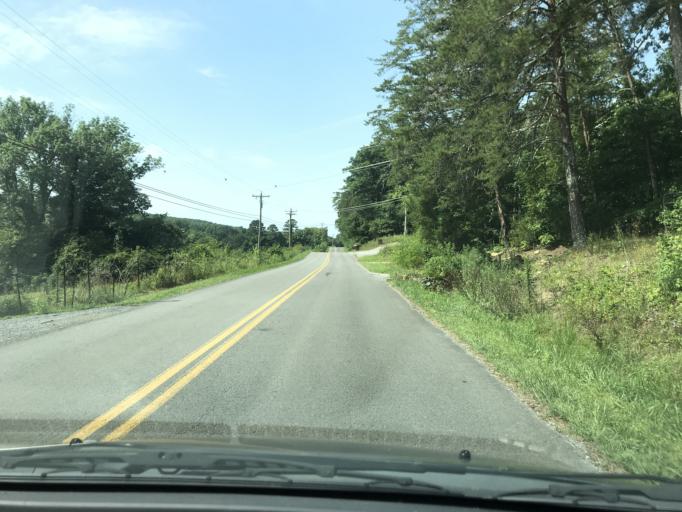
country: US
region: Tennessee
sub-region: Hamilton County
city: Apison
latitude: 35.0589
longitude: -84.9834
